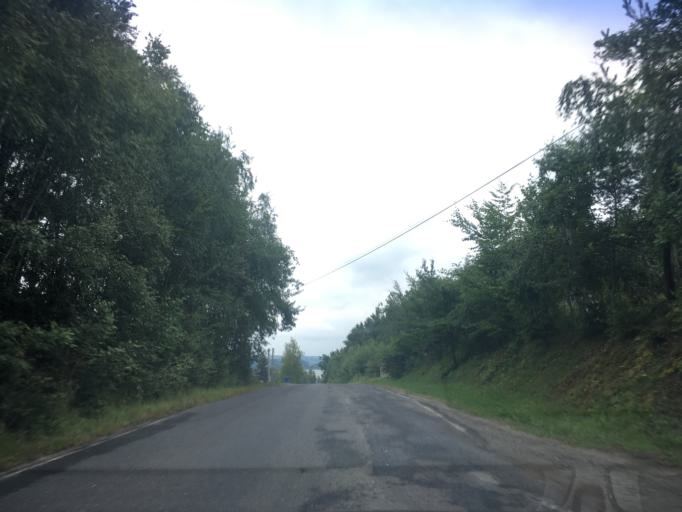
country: PL
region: Lesser Poland Voivodeship
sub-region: Powiat myslenicki
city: Brzaczowice
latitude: 49.8567
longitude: 20.0564
